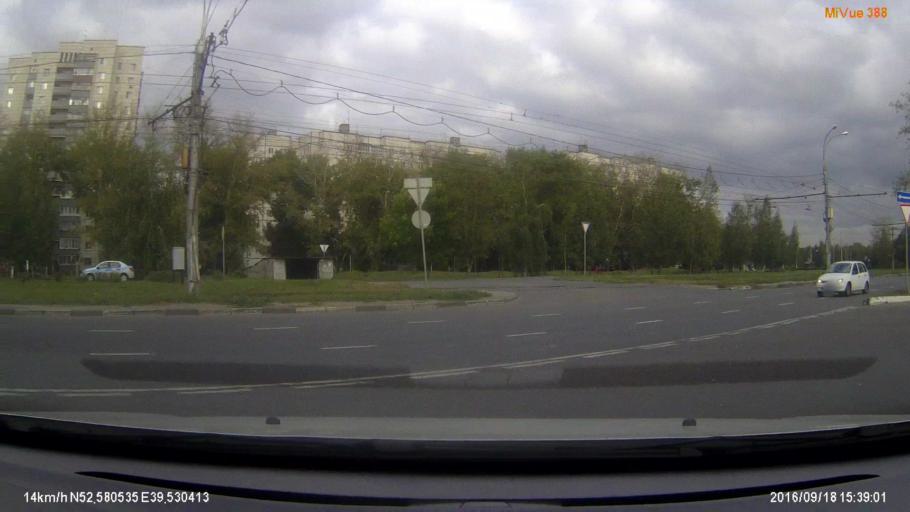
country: RU
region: Lipetsk
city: Syrskoye
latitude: 52.5806
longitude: 39.5301
